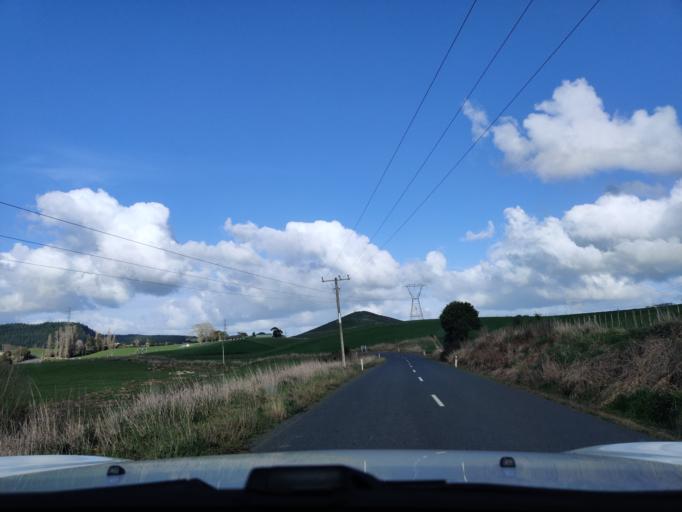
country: NZ
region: Waikato
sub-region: Waikato District
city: Te Kauwhata
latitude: -37.2846
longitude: 175.2115
